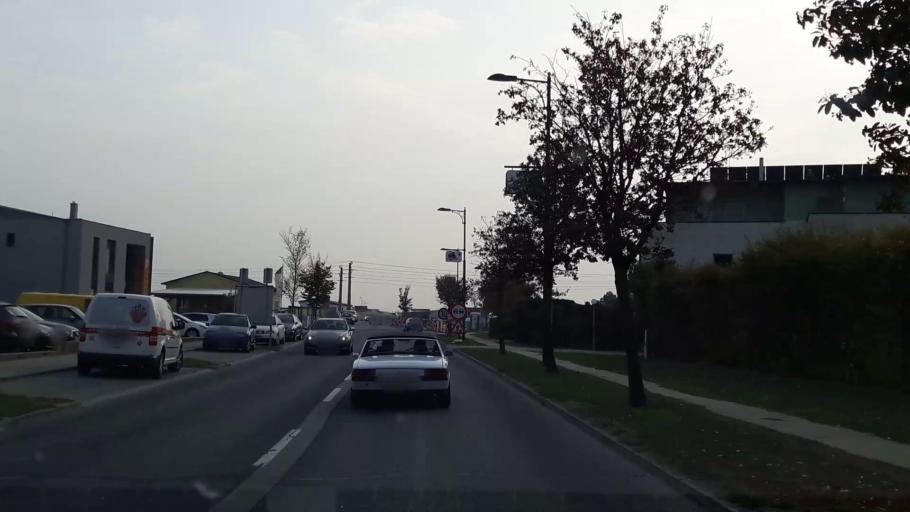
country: AT
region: Burgenland
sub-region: Politischer Bezirk Neusiedl am See
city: Parndorf
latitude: 47.9916
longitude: 16.8572
